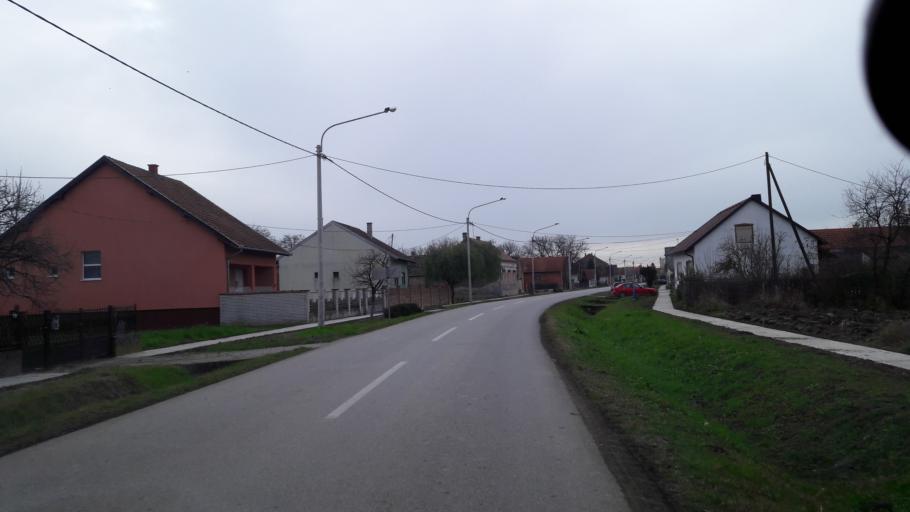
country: HR
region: Osjecko-Baranjska
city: Vladislavci
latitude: 45.4386
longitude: 18.5992
